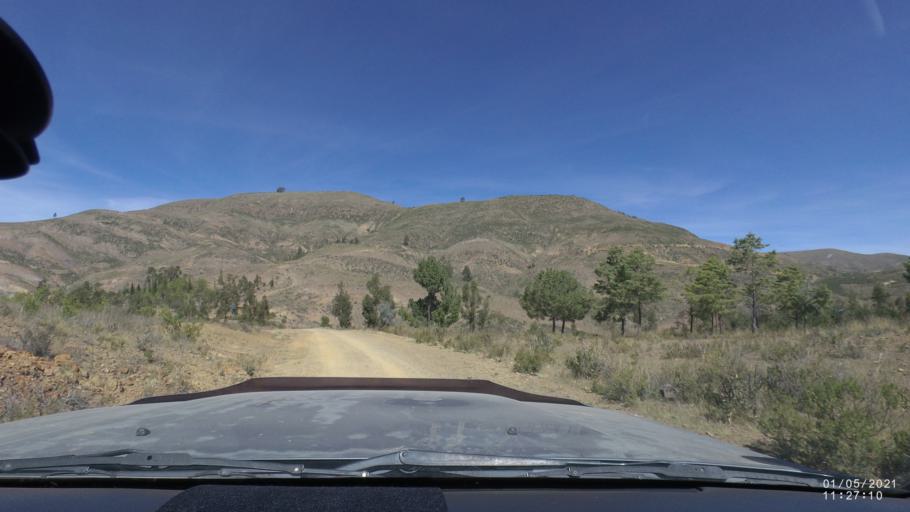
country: BO
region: Cochabamba
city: Tarata
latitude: -17.6560
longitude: -66.1313
